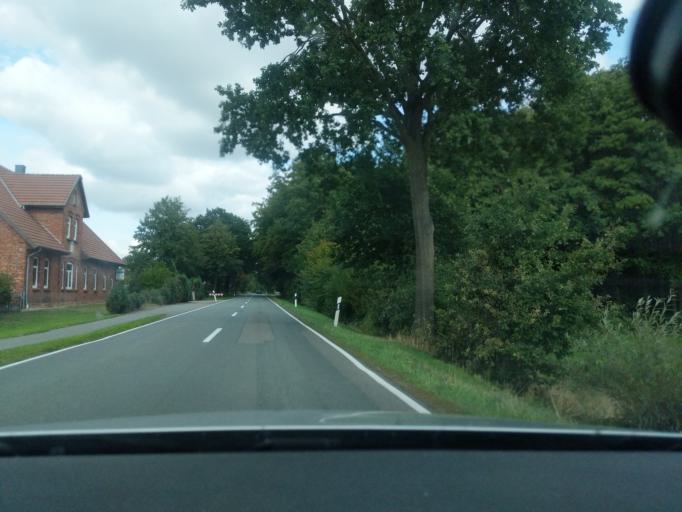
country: DE
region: Lower Saxony
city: Warpe
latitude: 52.7532
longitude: 9.0792
